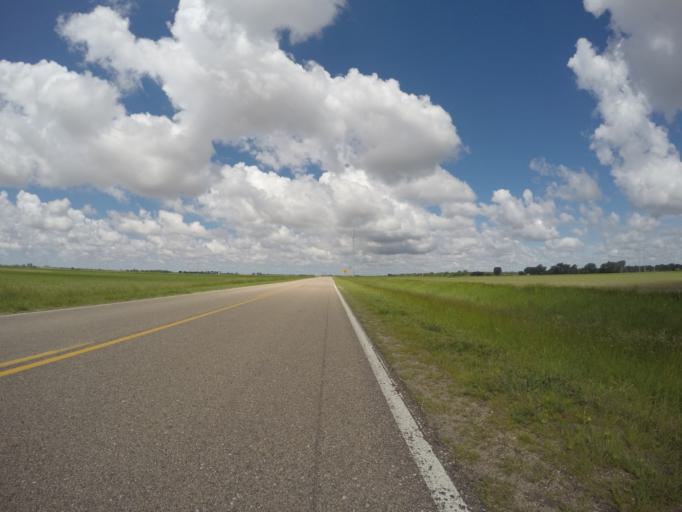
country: US
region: Nebraska
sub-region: Buffalo County
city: Kearney
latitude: 40.6570
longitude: -99.2538
